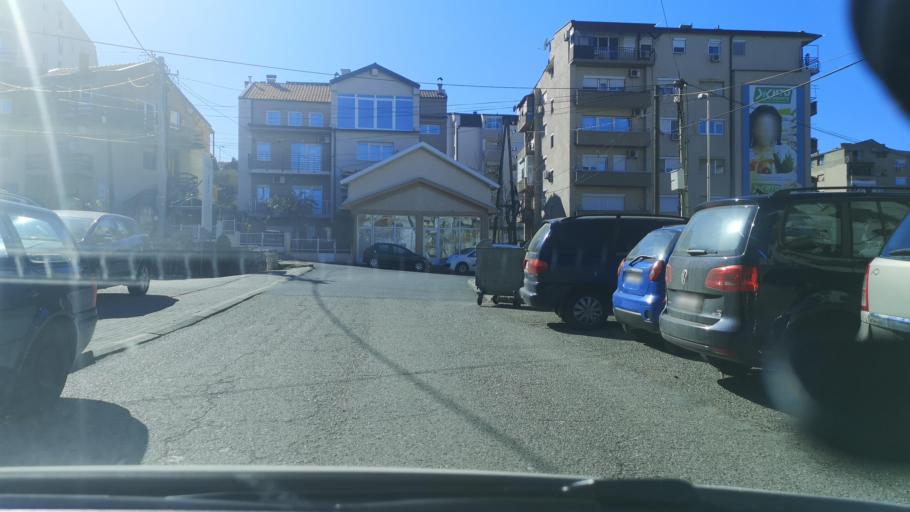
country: MK
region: Veles
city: Veles
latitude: 41.7149
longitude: 21.7698
